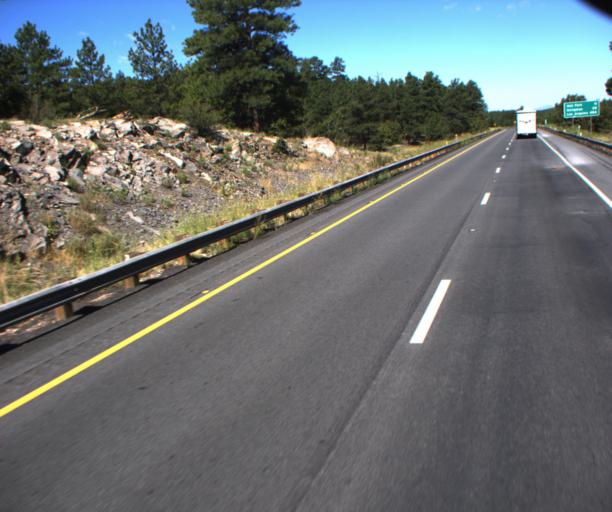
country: US
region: Arizona
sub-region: Coconino County
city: Williams
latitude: 35.2206
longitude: -112.2884
